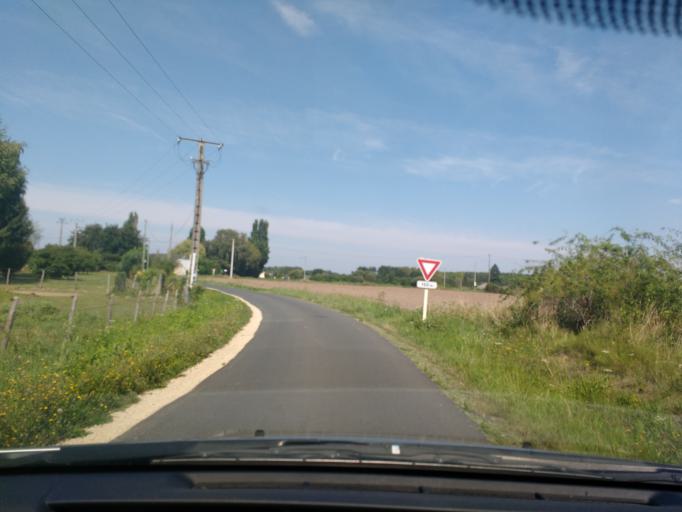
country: FR
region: Pays de la Loire
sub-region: Departement de Maine-et-Loire
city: Maze
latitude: 47.4649
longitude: -0.2919
